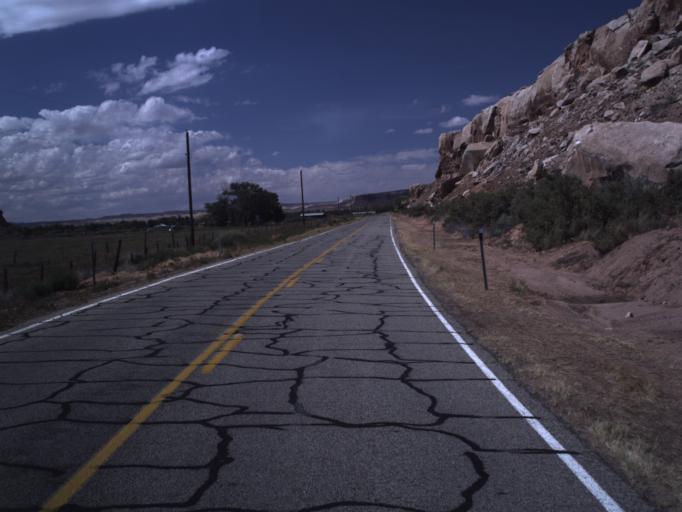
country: US
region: Utah
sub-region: San Juan County
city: Blanding
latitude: 37.2848
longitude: -109.5271
